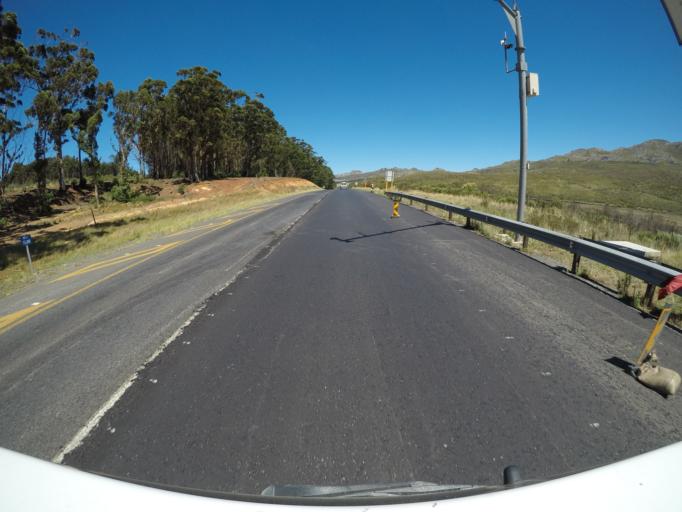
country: ZA
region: Western Cape
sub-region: Overberg District Municipality
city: Grabouw
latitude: -34.1523
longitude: 18.9474
